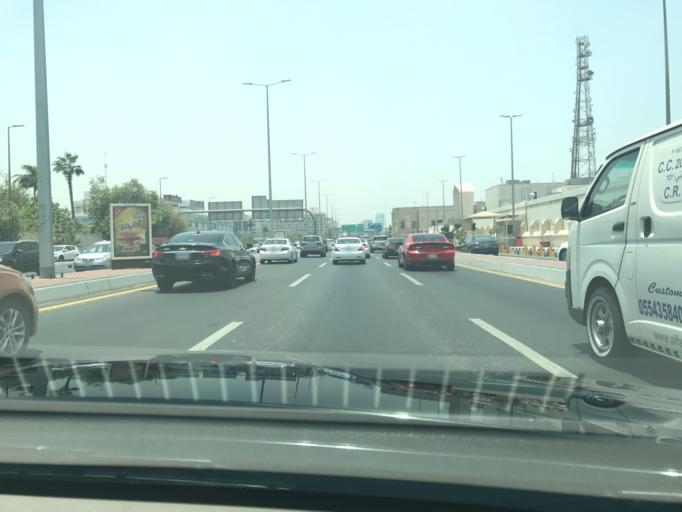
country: SA
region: Makkah
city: Jeddah
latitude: 21.5346
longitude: 39.1783
